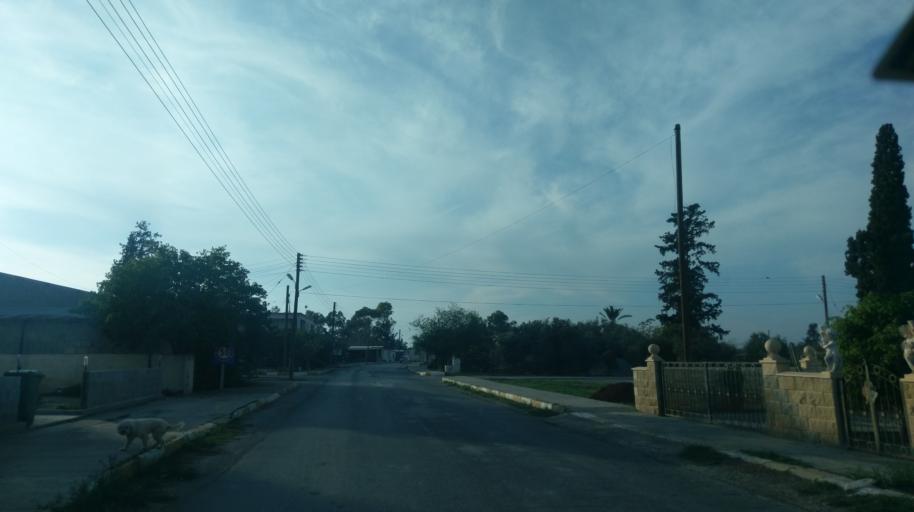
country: CY
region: Larnaka
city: Pergamos
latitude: 35.1059
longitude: 33.7127
